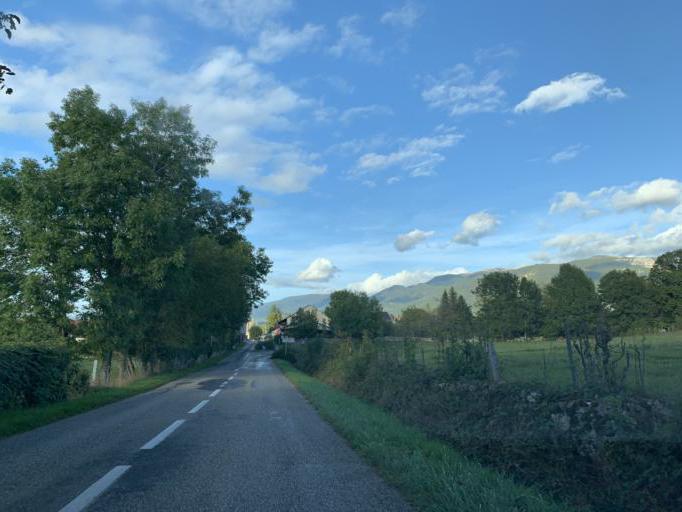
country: FR
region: Rhone-Alpes
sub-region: Departement de l'Ain
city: Virieu-le-Grand
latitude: 45.8473
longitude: 5.6788
